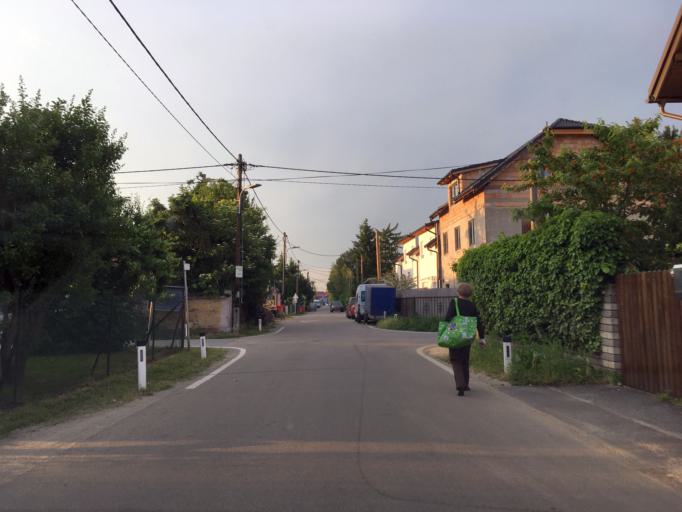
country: AT
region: Lower Austria
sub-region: Politischer Bezirk Wien-Umgebung
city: Gerasdorf bei Wien
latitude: 48.3136
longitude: 16.4943
